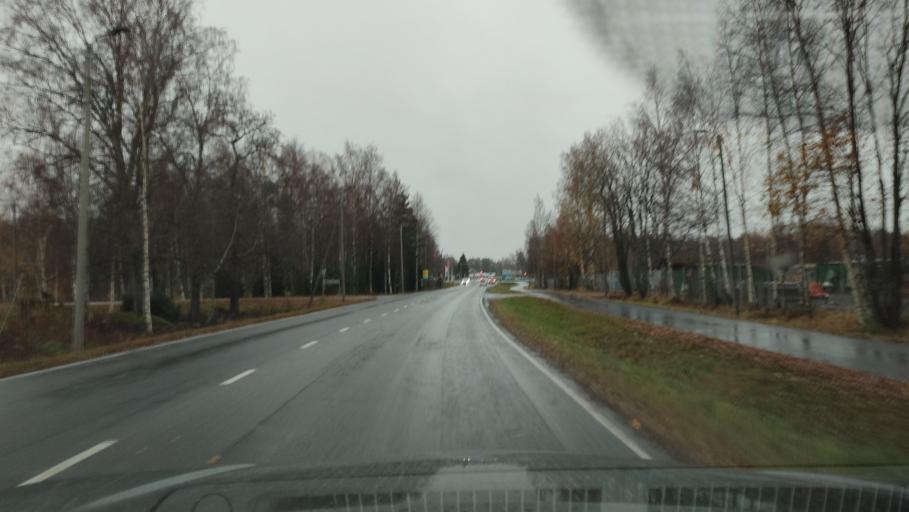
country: FI
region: Ostrobothnia
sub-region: Vaasa
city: Korsholm
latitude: 63.0920
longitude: 21.6532
